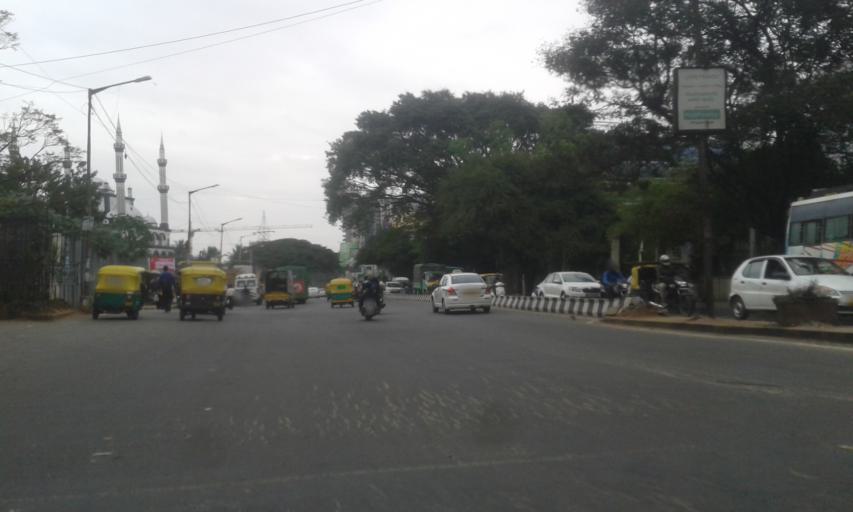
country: IN
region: Karnataka
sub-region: Bangalore Urban
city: Bangalore
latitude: 12.9187
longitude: 77.6000
